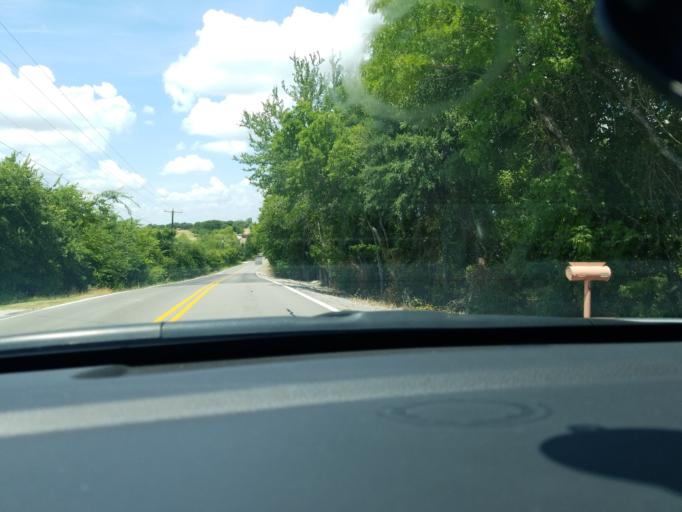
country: US
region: Texas
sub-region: Dallas County
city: Sunnyvale
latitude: 32.8139
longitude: -96.5749
